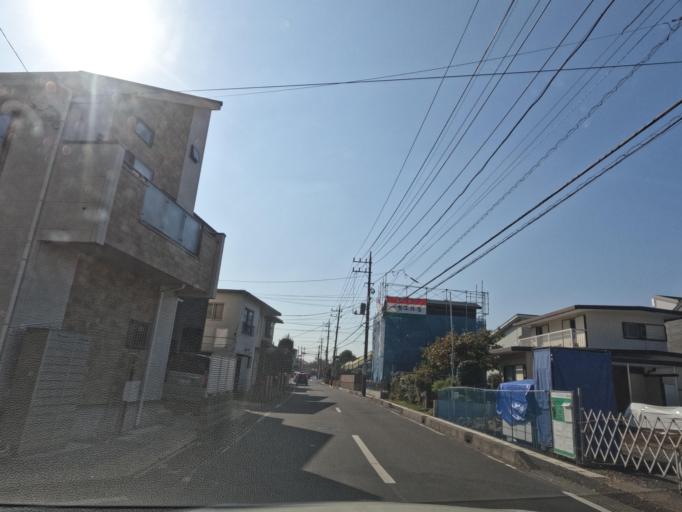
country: JP
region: Saitama
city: Ageoshimo
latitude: 35.9442
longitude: 139.6261
